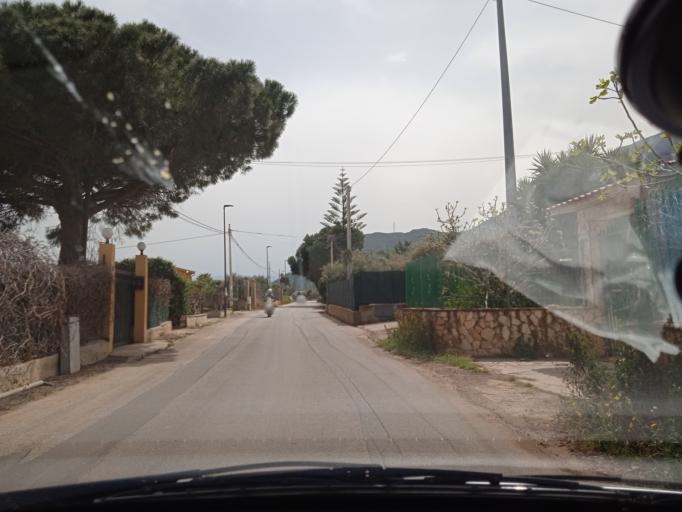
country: IT
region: Sicily
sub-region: Palermo
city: Torre Colonna-Sperone
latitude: 38.0329
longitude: 13.5650
